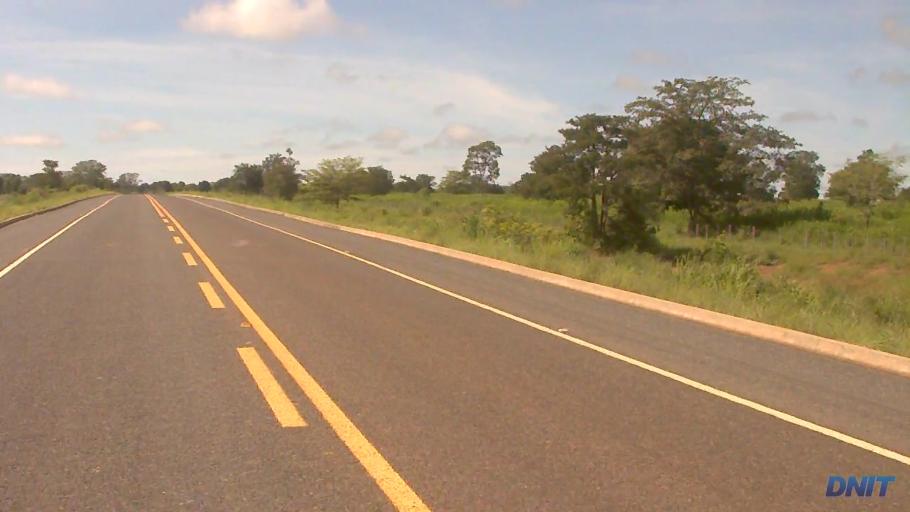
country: BR
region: Goias
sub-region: Sao Miguel Do Araguaia
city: Sao Miguel do Araguaia
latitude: -13.3015
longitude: -50.1747
